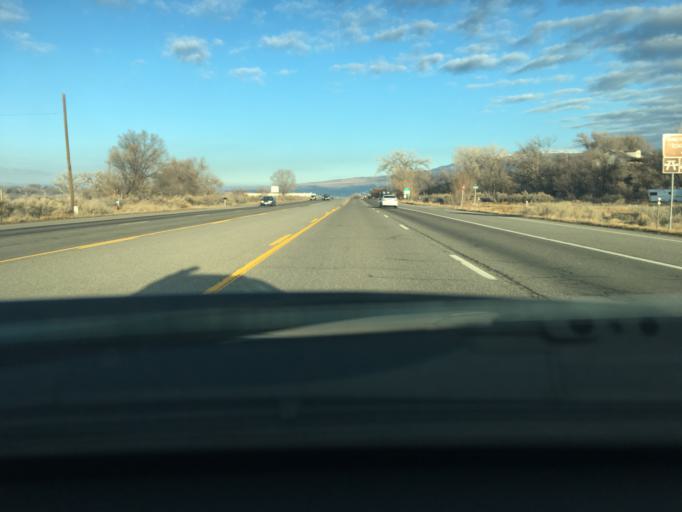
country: US
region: Colorado
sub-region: Delta County
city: Delta
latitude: 38.7139
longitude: -108.0514
